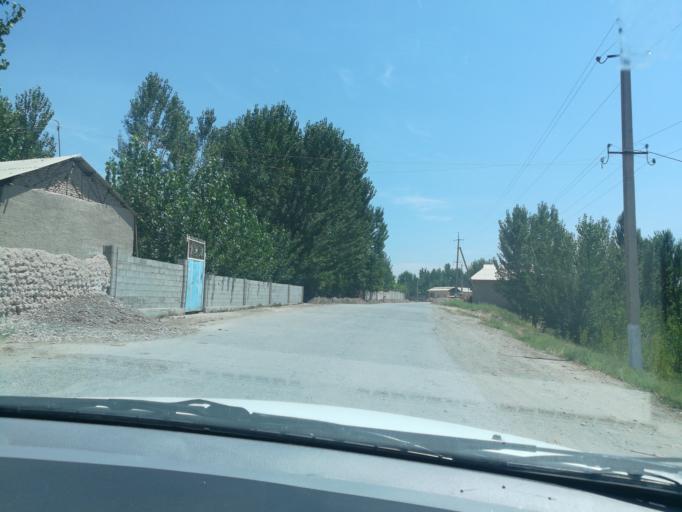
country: UZ
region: Namangan
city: Haqqulobod
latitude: 40.8979
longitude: 72.0069
